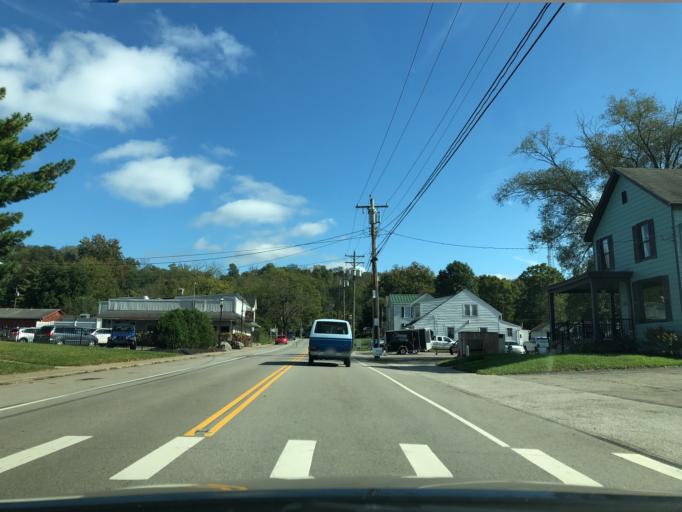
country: US
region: Ohio
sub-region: Hamilton County
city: The Village of Indian Hill
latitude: 39.2464
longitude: -84.2942
